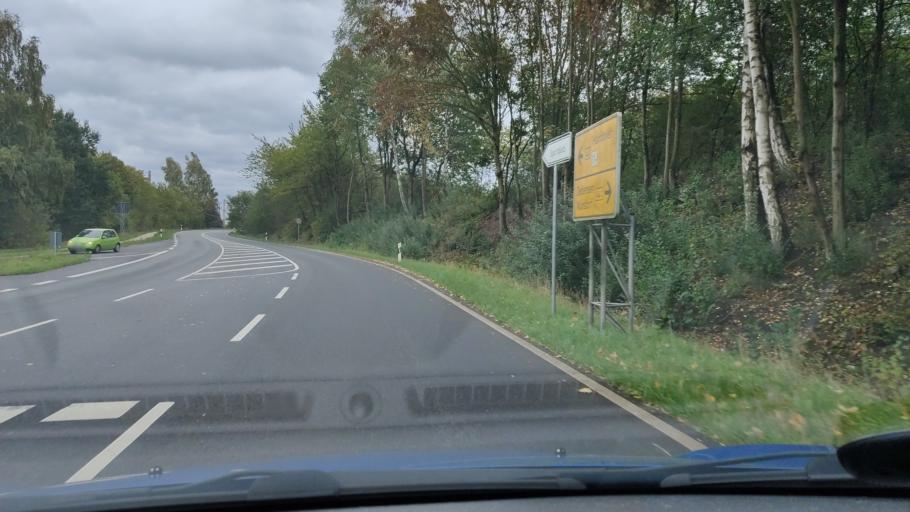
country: DE
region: Lower Saxony
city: Garbsen
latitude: 52.4035
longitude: 9.5339
